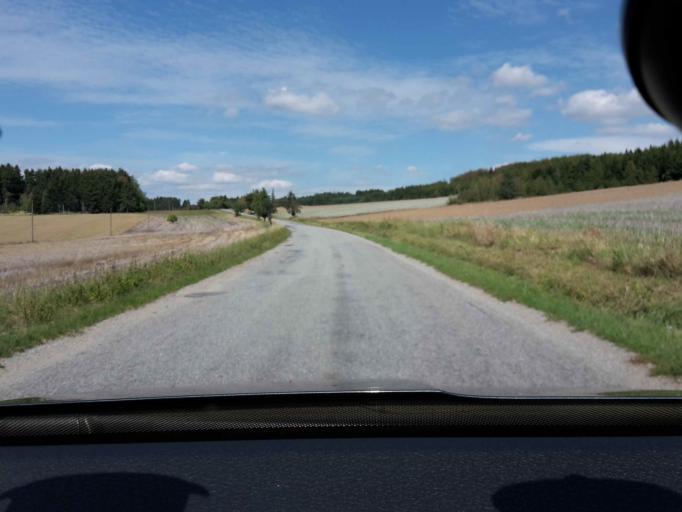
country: CZ
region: Vysocina
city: Zeletava
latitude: 49.1234
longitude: 15.6087
